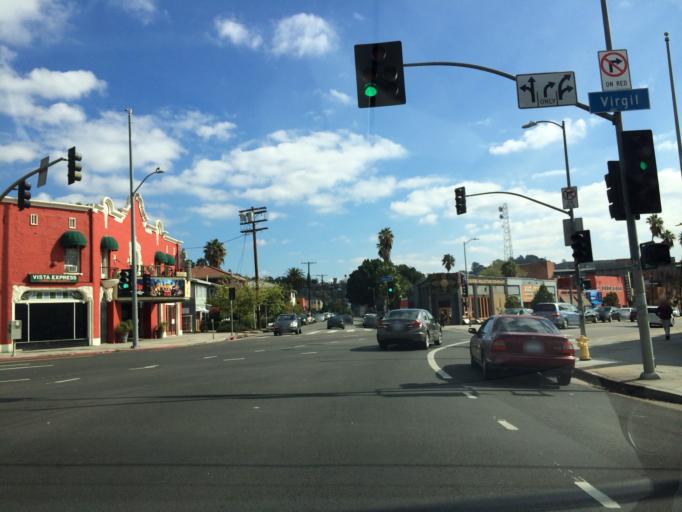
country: US
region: California
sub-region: Los Angeles County
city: Silver Lake
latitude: 34.0982
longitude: -118.2874
